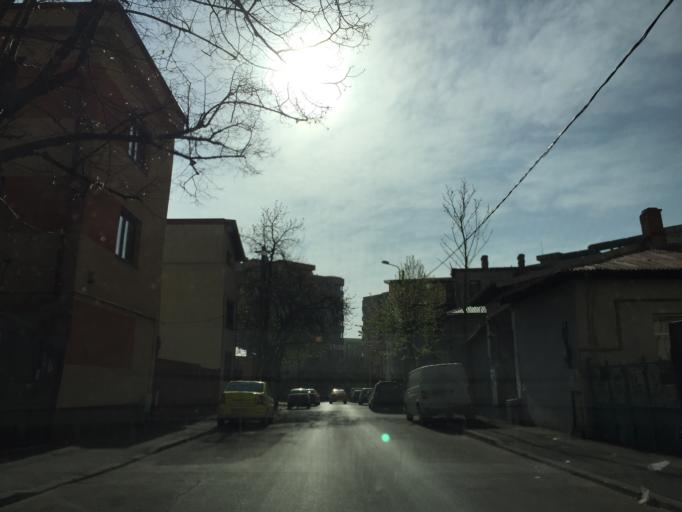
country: RO
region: Bucuresti
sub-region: Municipiul Bucuresti
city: Bucharest
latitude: 44.4197
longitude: 26.1204
